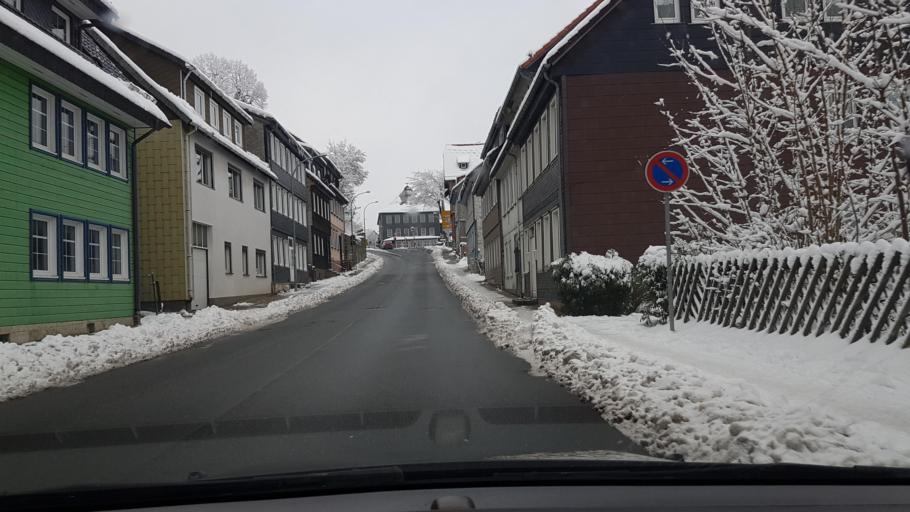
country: DE
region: Lower Saxony
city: Clausthal-Zellerfeld
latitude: 51.8044
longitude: 10.3307
